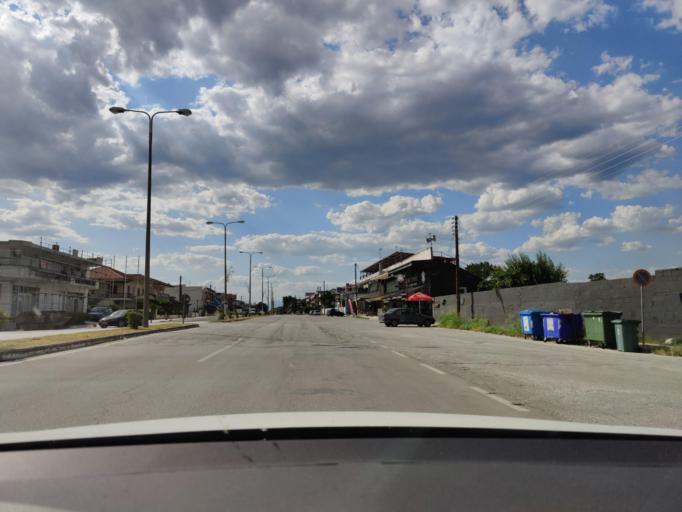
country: GR
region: Central Macedonia
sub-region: Nomos Serron
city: Lefkonas
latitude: 41.0955
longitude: 23.5030
